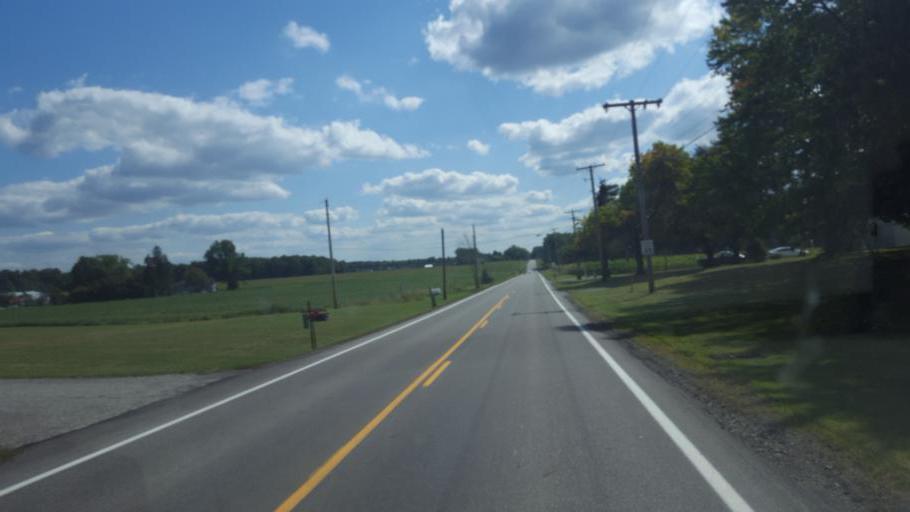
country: US
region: Ohio
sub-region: Wayne County
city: West Salem
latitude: 40.9420
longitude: -82.2147
